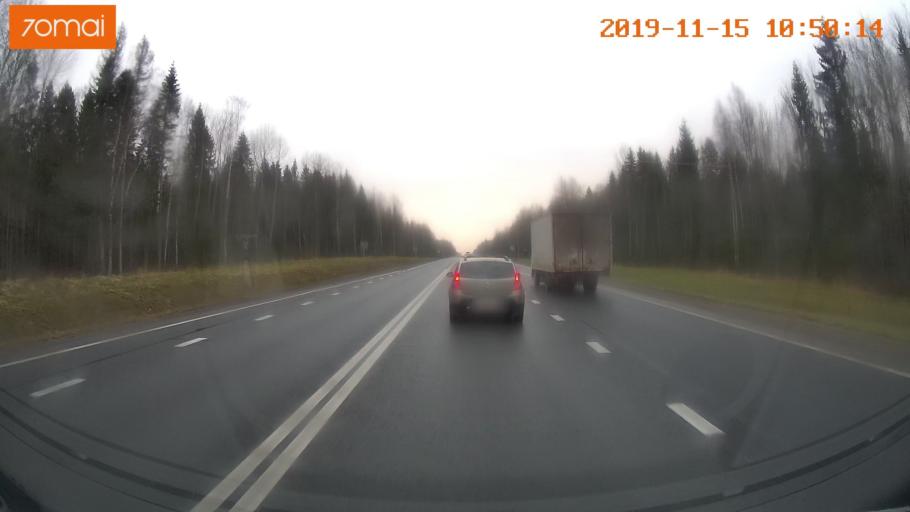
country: RU
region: Vologda
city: Chebsara
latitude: 59.1864
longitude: 38.6765
